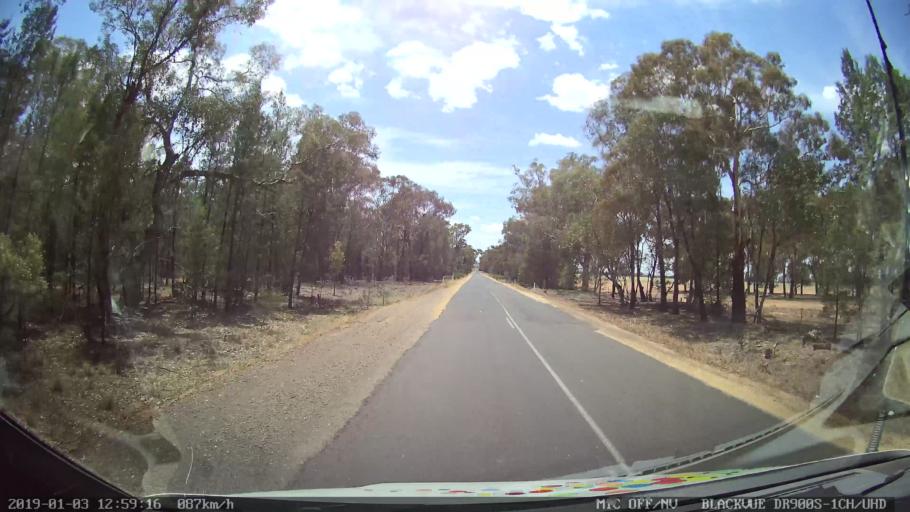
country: AU
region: New South Wales
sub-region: Cabonne
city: Canowindra
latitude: -33.6381
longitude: 148.3871
